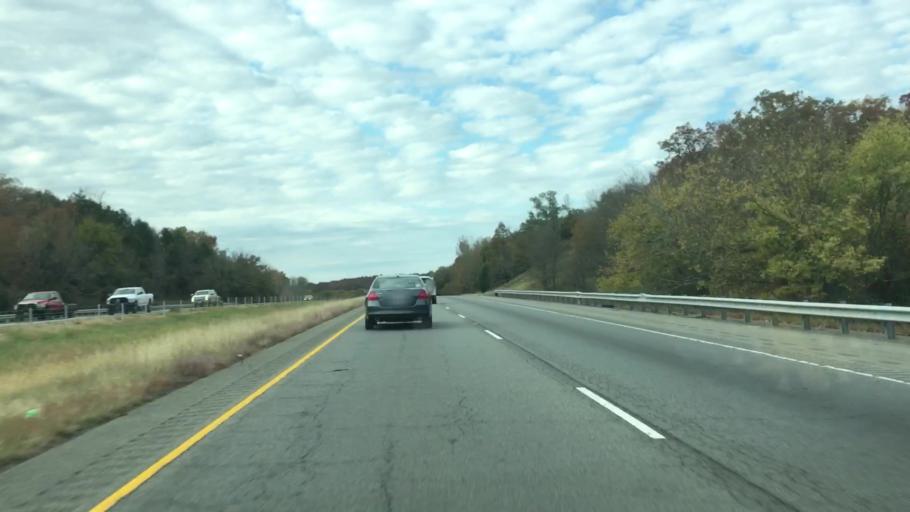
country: US
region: Arkansas
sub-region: Faulkner County
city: Conway
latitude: 35.1341
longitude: -92.5180
